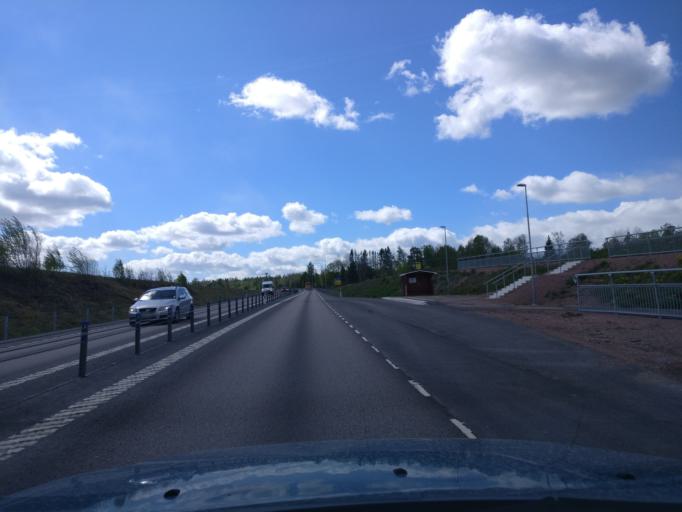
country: SE
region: Vaermland
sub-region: Karlstads Kommun
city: Karlstad
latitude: 59.4520
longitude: 13.5528
